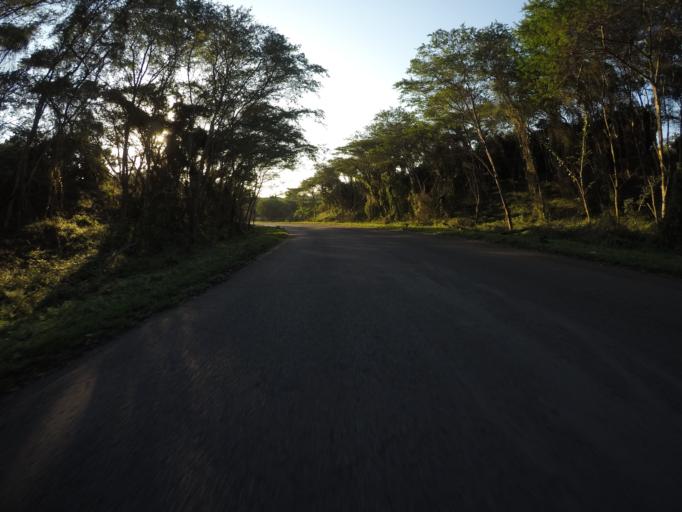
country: ZA
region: KwaZulu-Natal
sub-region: uThungulu District Municipality
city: KwaMbonambi
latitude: -28.6938
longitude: 32.2106
